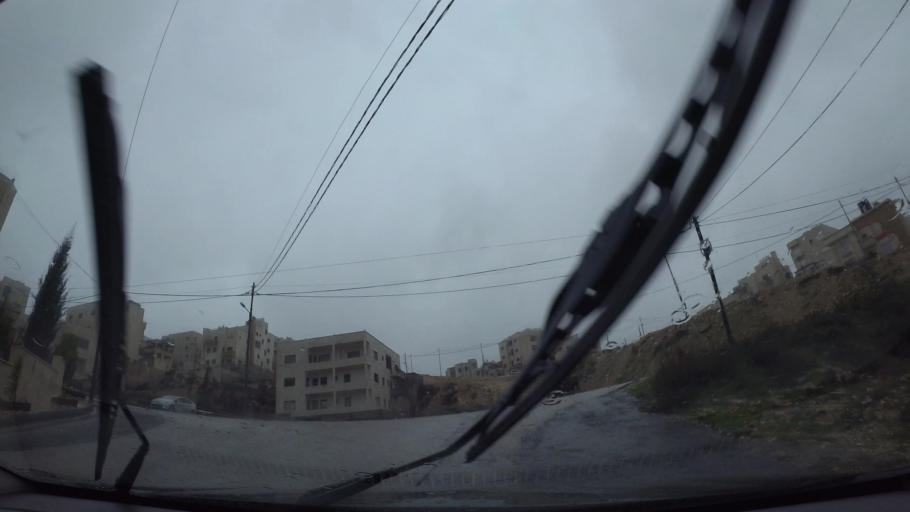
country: JO
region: Amman
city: Al Jubayhah
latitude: 32.0106
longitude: 35.8993
